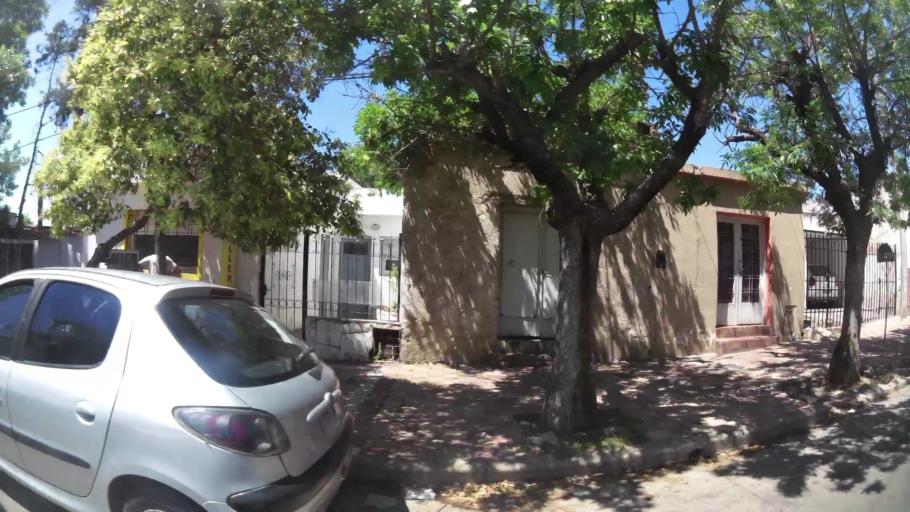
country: AR
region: Cordoba
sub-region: Departamento de Capital
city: Cordoba
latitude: -31.4297
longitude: -64.2026
